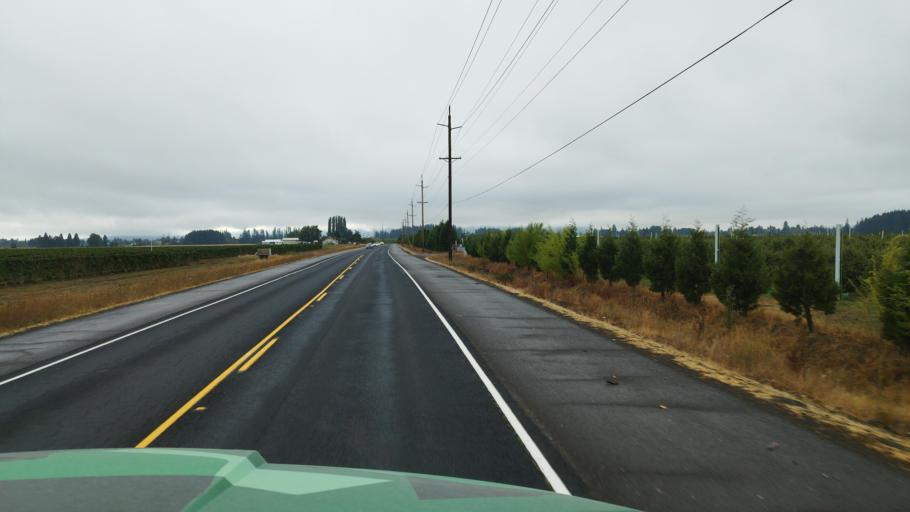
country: US
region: Oregon
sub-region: Washington County
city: Cornelius
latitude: 45.5470
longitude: -123.0735
